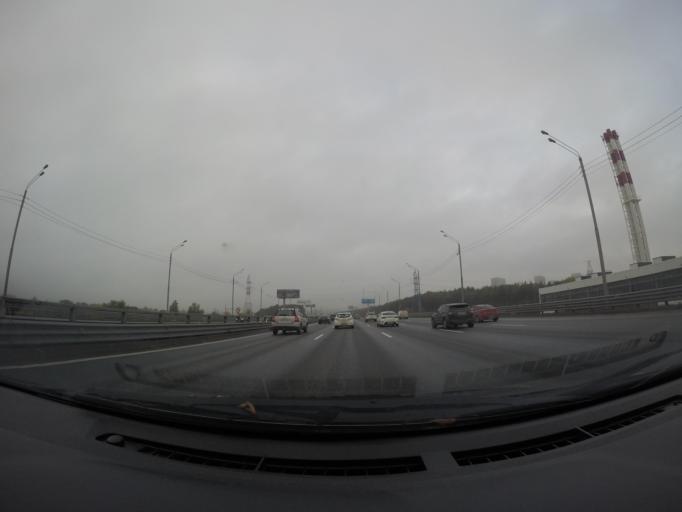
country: RU
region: Moscow
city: Rublevo
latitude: 55.7956
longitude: 37.3522
